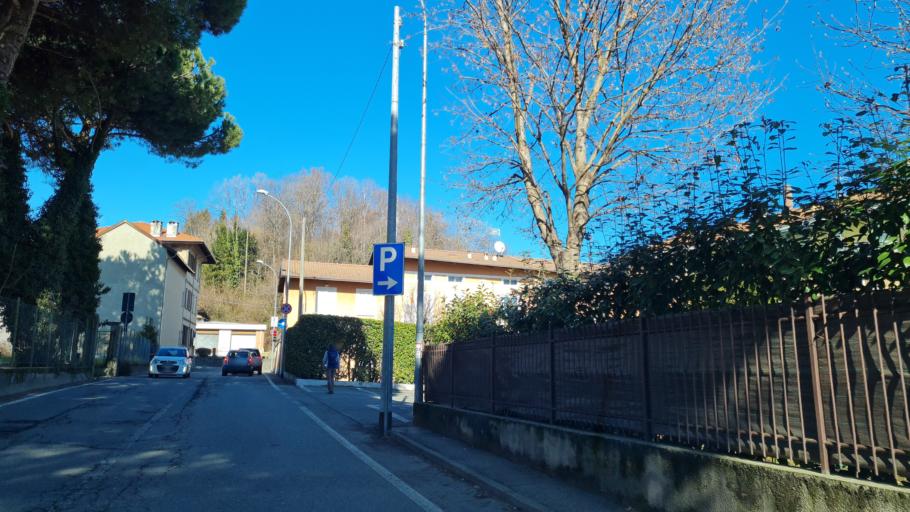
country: IT
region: Piedmont
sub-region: Provincia di Biella
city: Occhieppo Inferiore
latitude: 45.5551
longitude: 8.0278
